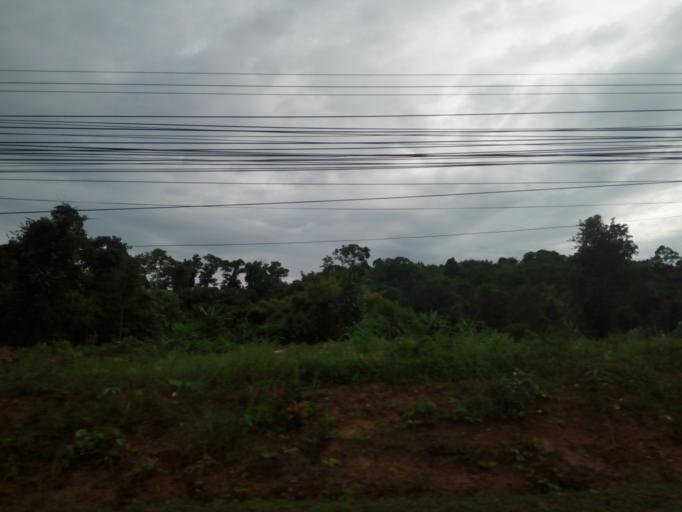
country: TH
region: Phuket
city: Thalang
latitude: 8.0905
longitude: 98.3321
